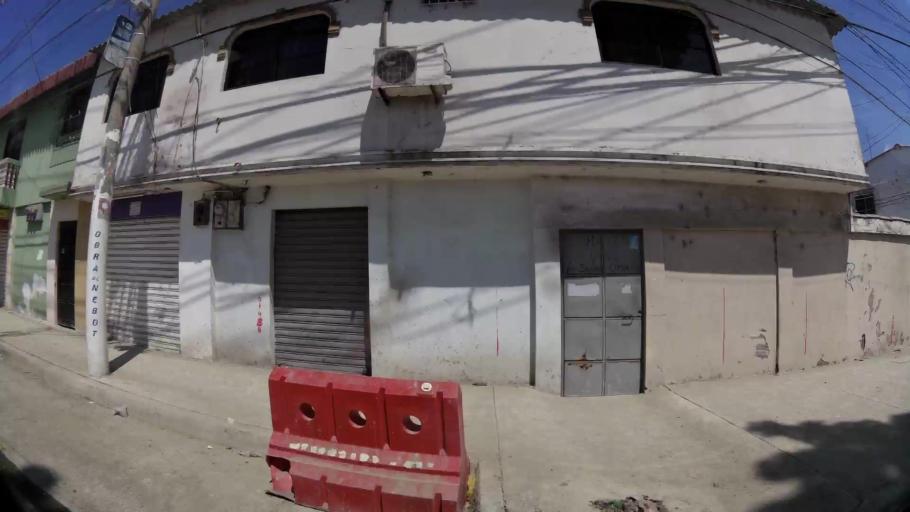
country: EC
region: Guayas
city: Eloy Alfaro
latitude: -2.1132
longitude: -79.9027
